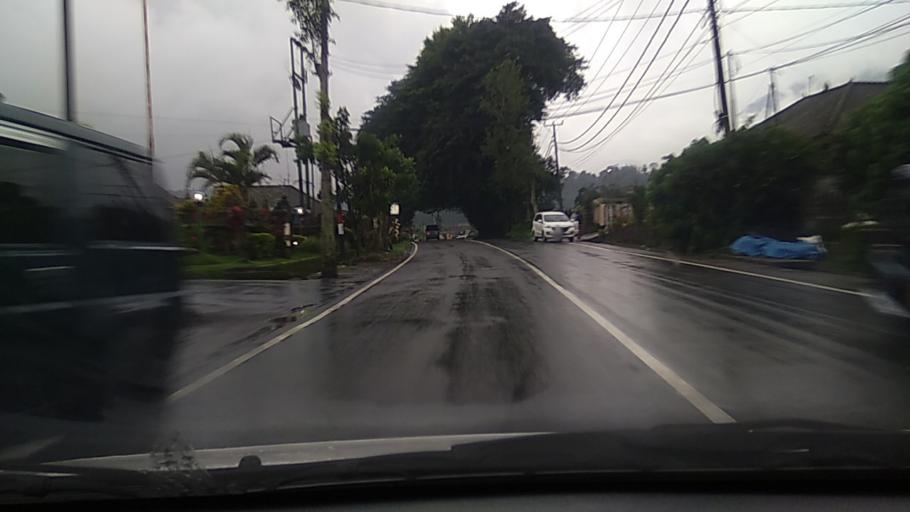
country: ID
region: Bali
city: Munduk
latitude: -8.2681
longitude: 115.1637
